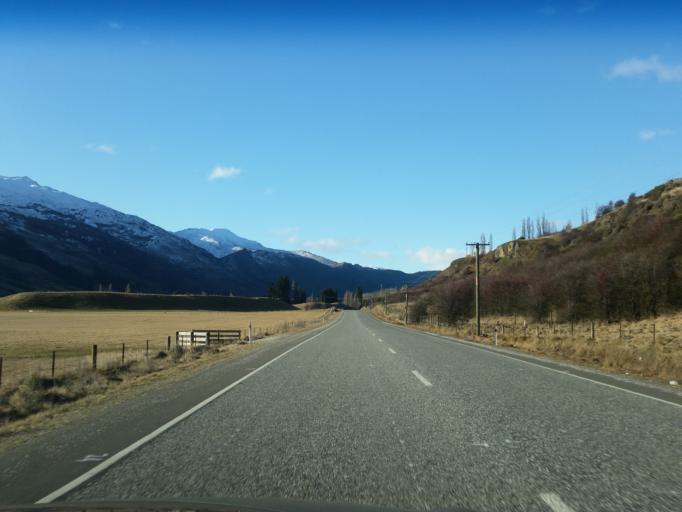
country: NZ
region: Otago
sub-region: Queenstown-Lakes District
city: Queenstown
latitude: -44.9648
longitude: 168.7138
